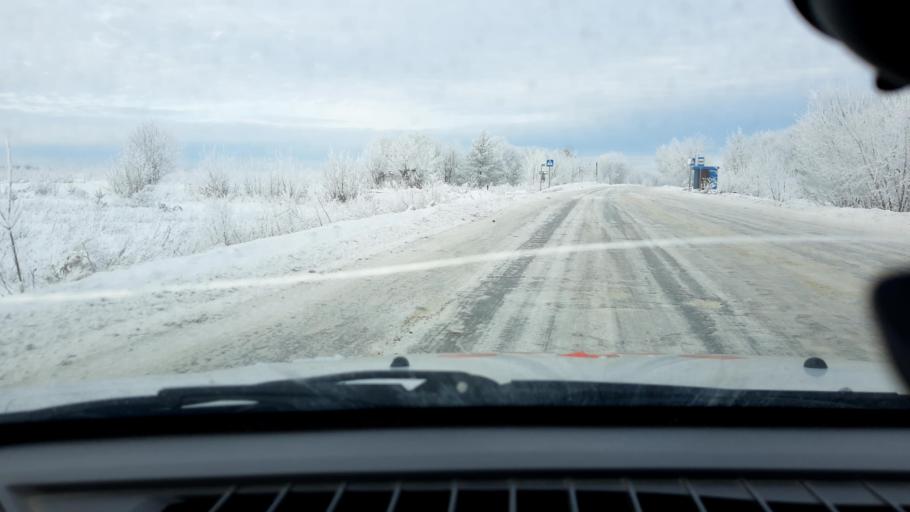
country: RU
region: Nizjnij Novgorod
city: Bogorodsk
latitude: 56.0685
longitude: 43.5812
